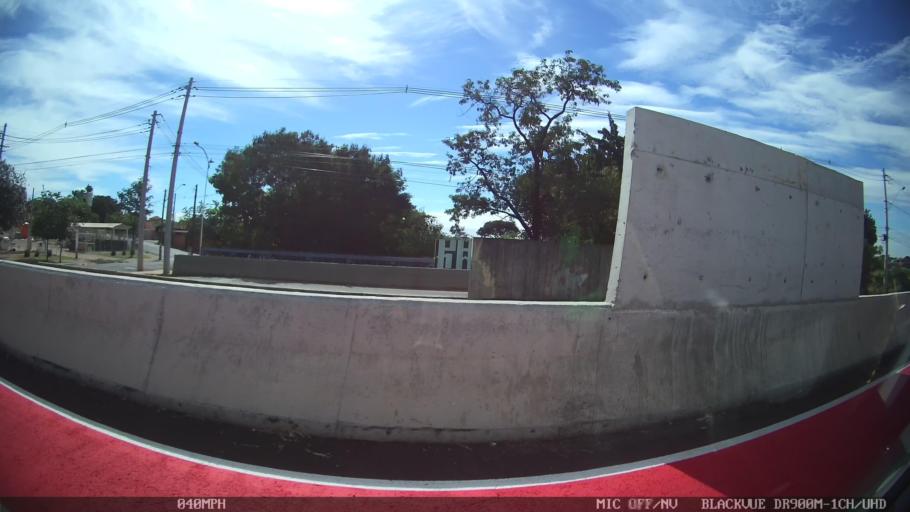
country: BR
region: Sao Paulo
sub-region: Sao Jose Do Rio Preto
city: Sao Jose do Rio Preto
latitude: -20.8251
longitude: -49.3481
